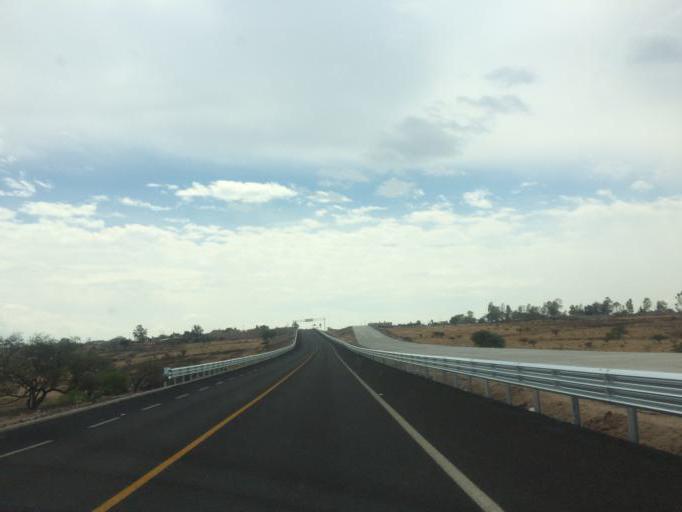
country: MX
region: Guanajuato
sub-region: Silao de la Victoria
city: El Refugio de los Sauces
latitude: 21.0457
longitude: -101.5240
